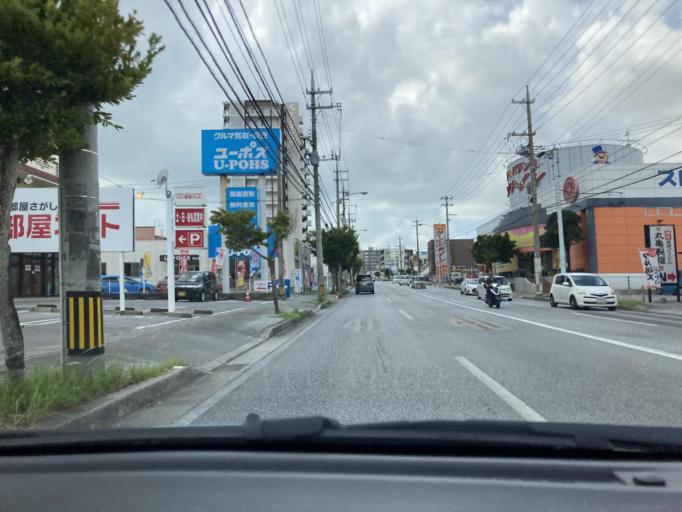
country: JP
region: Okinawa
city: Okinawa
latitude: 26.3447
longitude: 127.8211
